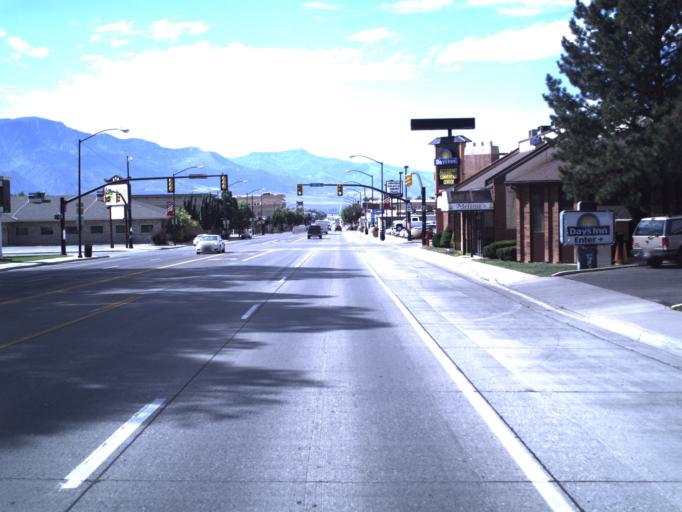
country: US
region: Utah
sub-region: Sevier County
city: Richfield
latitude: 38.7731
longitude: -112.0849
